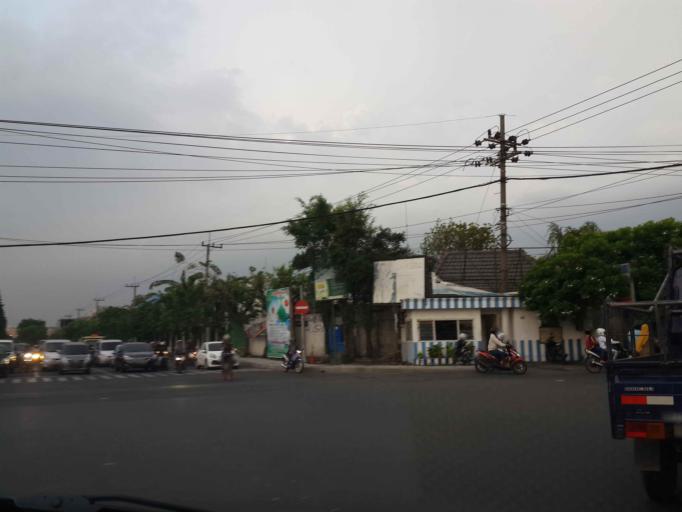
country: ID
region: East Java
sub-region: Kota Surabaya
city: Surabaya
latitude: -7.2453
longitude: 112.7209
